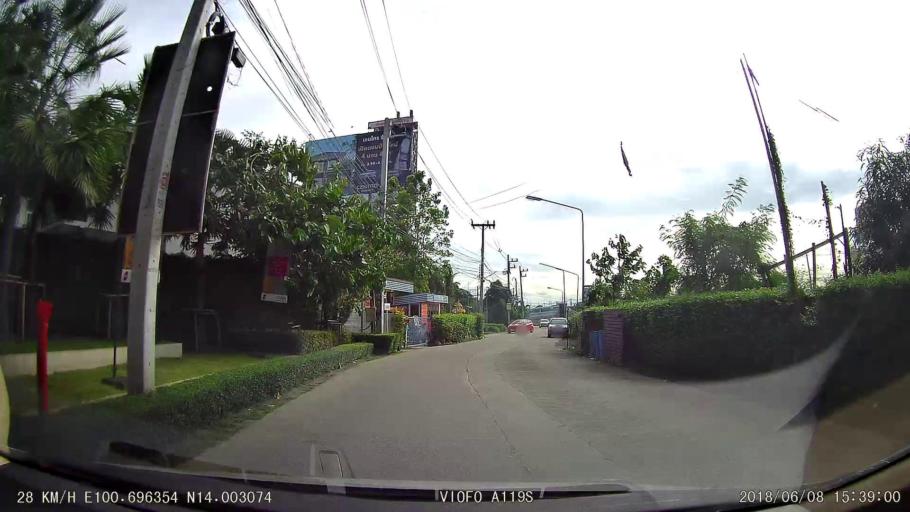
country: TH
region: Pathum Thani
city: Thanyaburi
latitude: 14.0030
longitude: 100.6962
